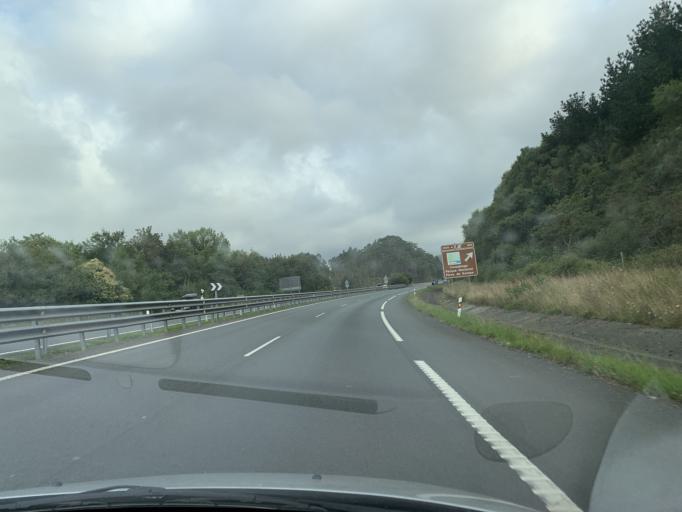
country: ES
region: Asturias
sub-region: Province of Asturias
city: Llanes
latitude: 43.4403
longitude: -4.8736
